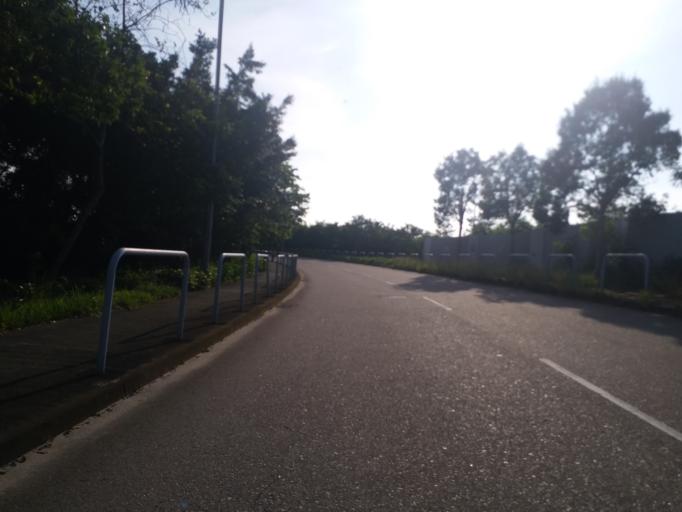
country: HK
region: Yuen Long
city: Yuen Long Kau Hui
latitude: 22.4793
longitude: 114.0556
